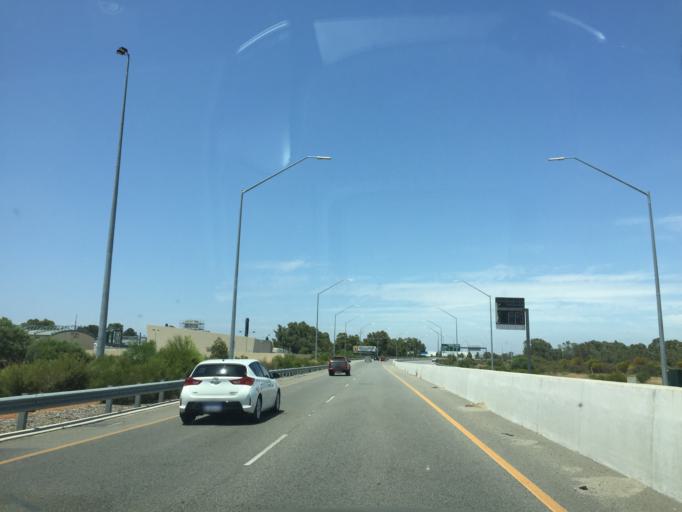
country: AU
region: Western Australia
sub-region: Belmont
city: Kewdale
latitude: -31.9585
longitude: 115.9682
